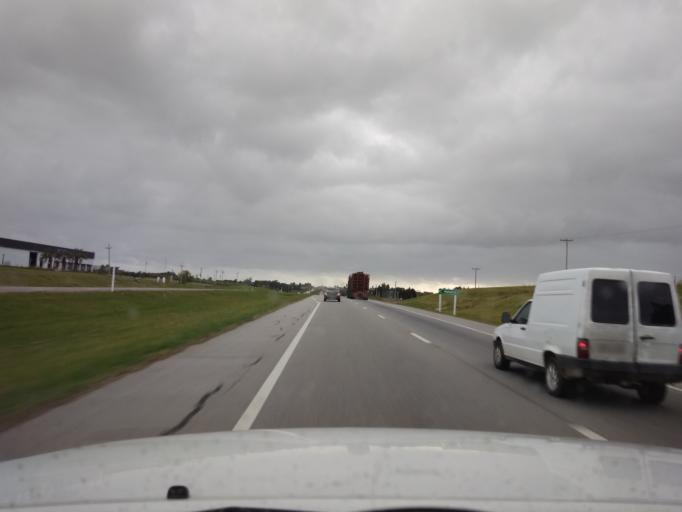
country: UY
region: Canelones
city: Las Piedras
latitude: -34.7028
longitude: -56.2405
